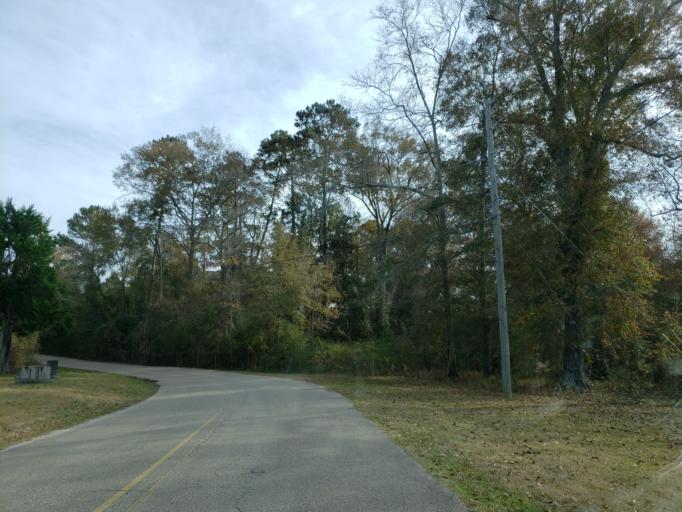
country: US
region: Mississippi
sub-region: Forrest County
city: Glendale
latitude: 31.3498
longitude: -89.3206
